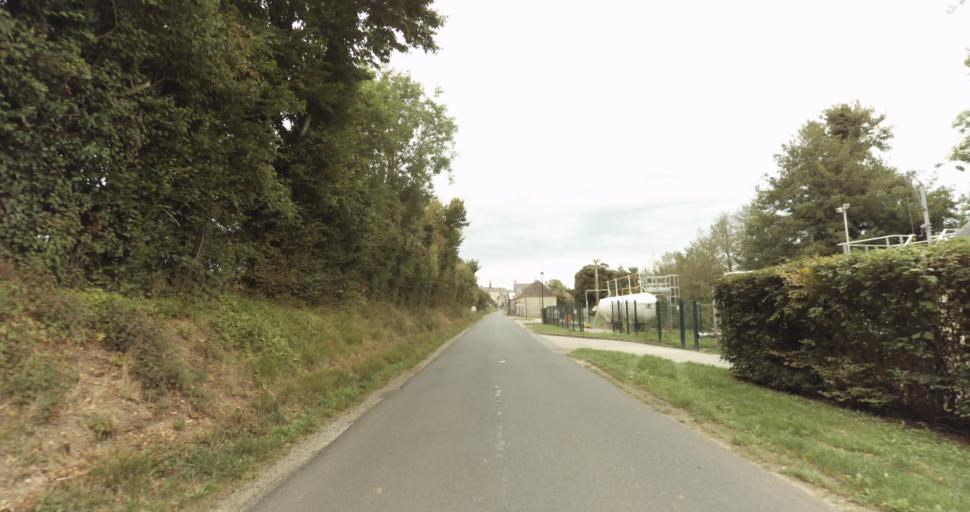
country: FR
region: Lower Normandy
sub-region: Departement de l'Orne
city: Gace
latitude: 48.6973
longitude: 0.2799
